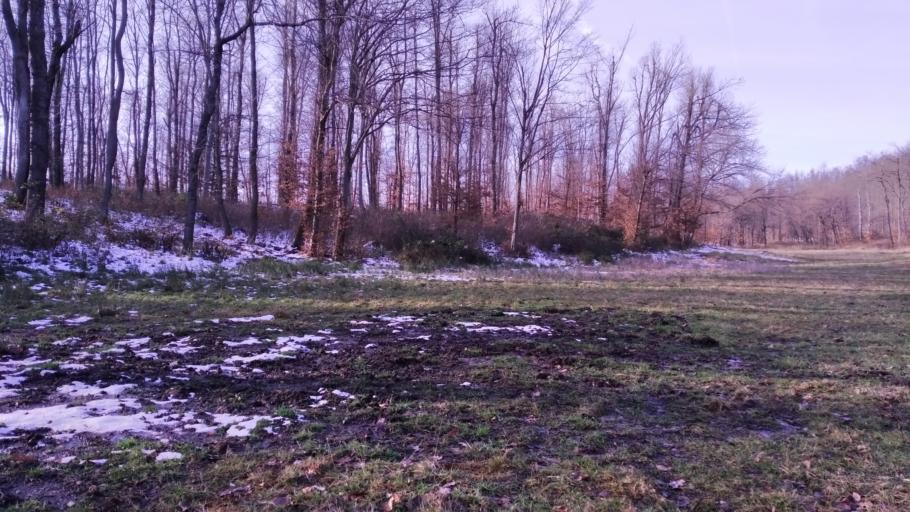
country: HU
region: Pest
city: Pilisszentkereszt
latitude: 47.7106
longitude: 18.8874
